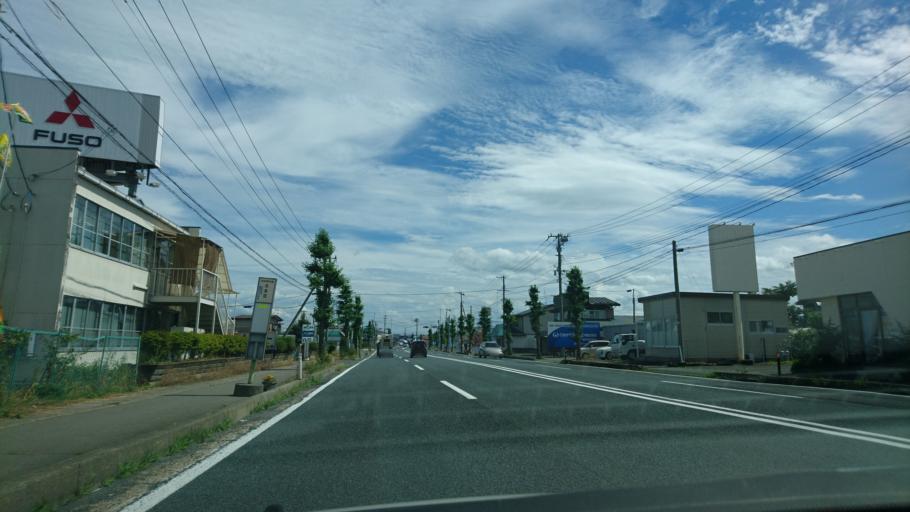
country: JP
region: Iwate
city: Morioka-shi
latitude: 39.6289
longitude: 141.1743
